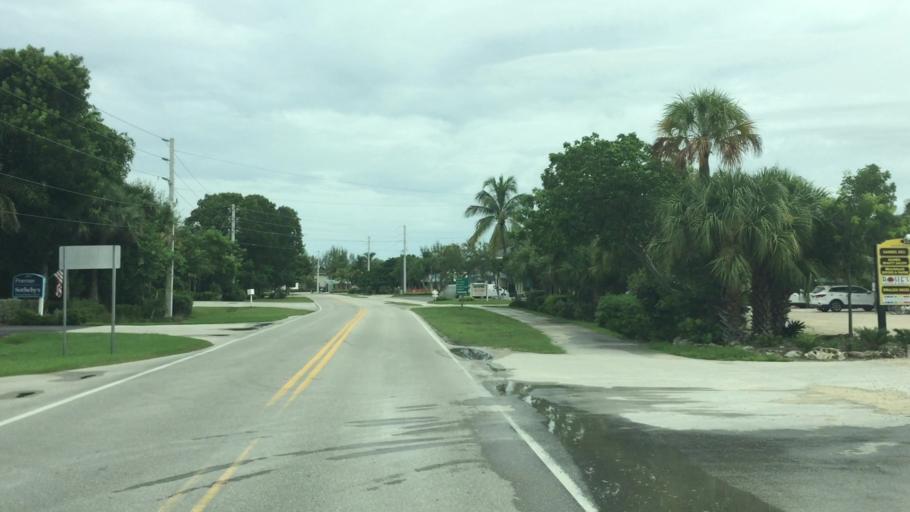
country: US
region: Florida
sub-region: Lee County
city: Sanibel
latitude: 26.4372
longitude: -82.0772
